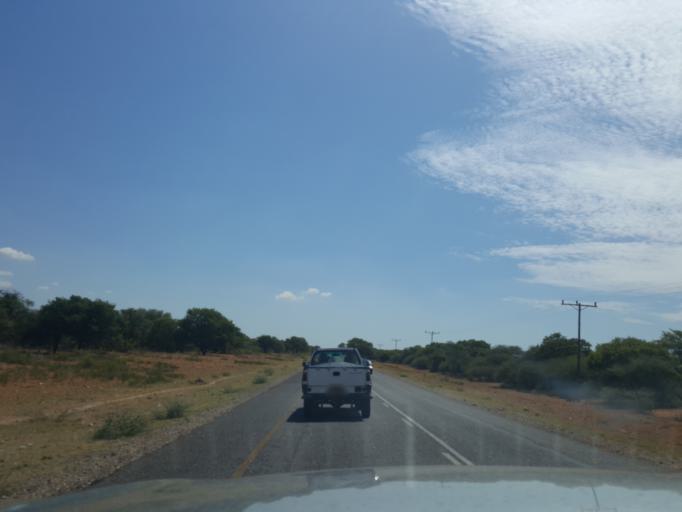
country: BW
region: Kweneng
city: Letlhakeng
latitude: -24.1235
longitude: 25.0950
